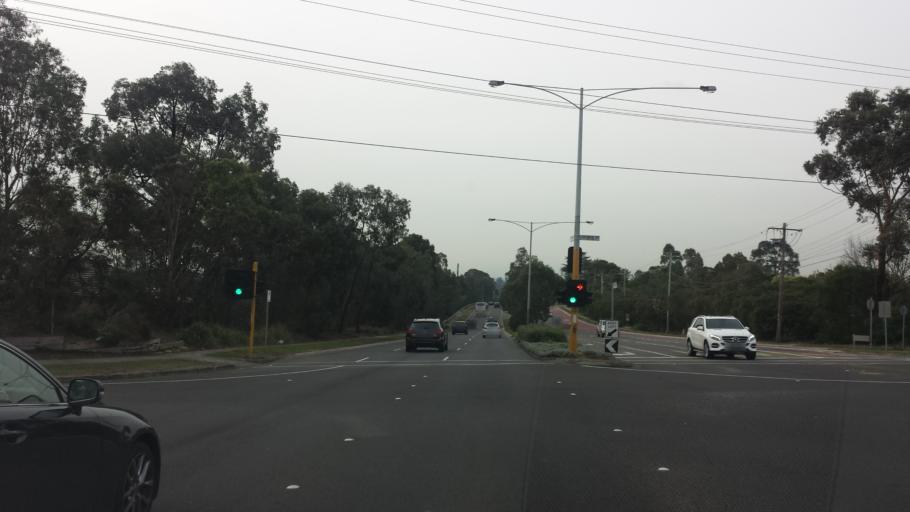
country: AU
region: Victoria
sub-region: Manningham
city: Doncaster
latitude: -37.7778
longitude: 145.1242
